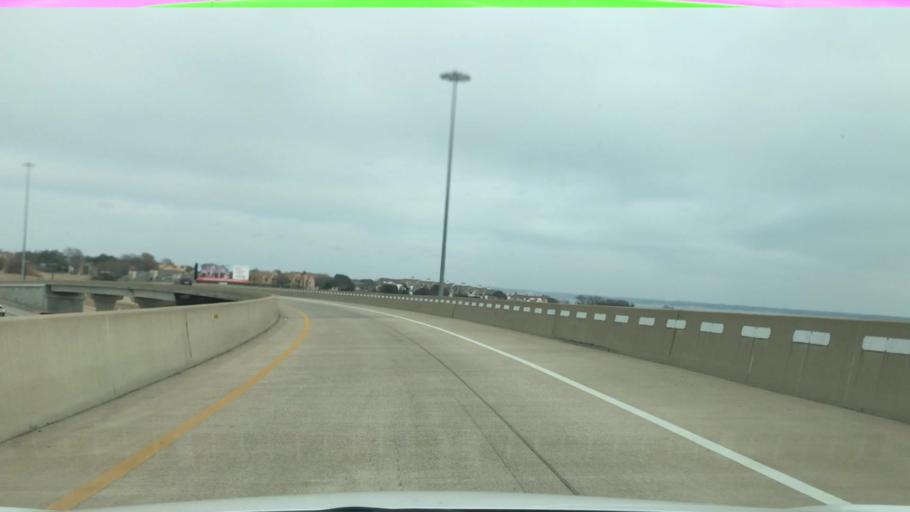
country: US
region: Texas
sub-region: Dallas County
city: Rowlett
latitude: 32.8587
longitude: -96.5519
